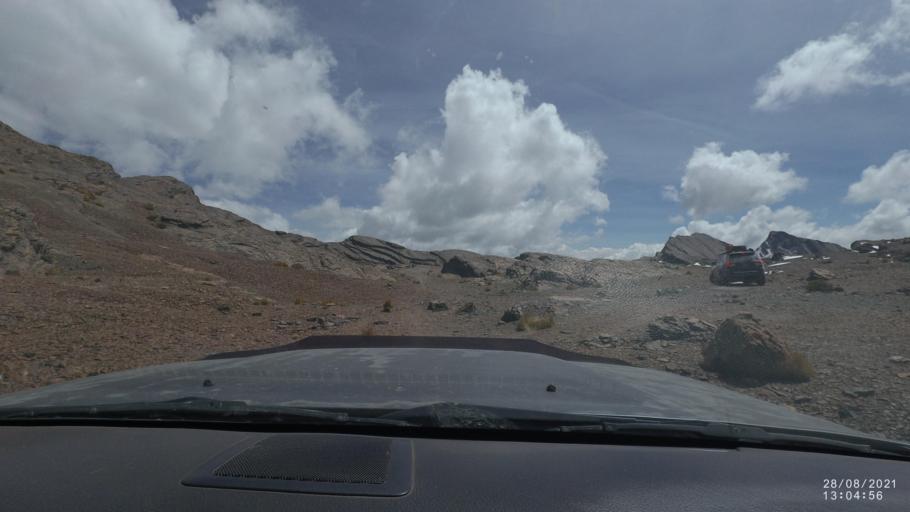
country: BO
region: Cochabamba
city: Sipe Sipe
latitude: -17.2830
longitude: -66.3890
